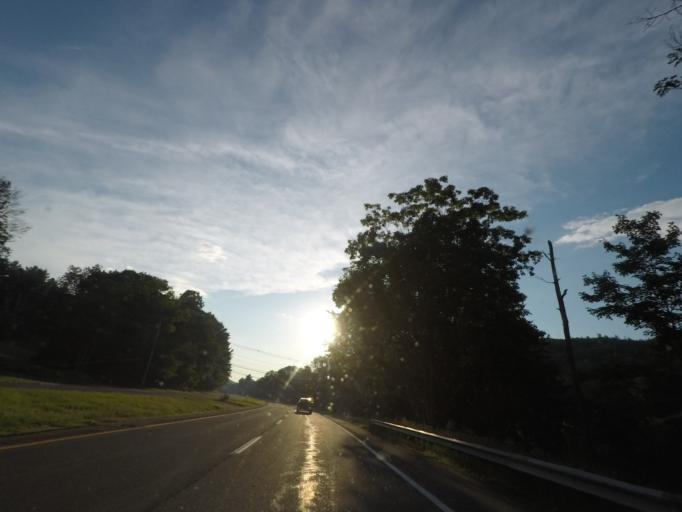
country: US
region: Massachusetts
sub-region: Hampden County
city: Brimfield
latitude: 42.1187
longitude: -72.2392
